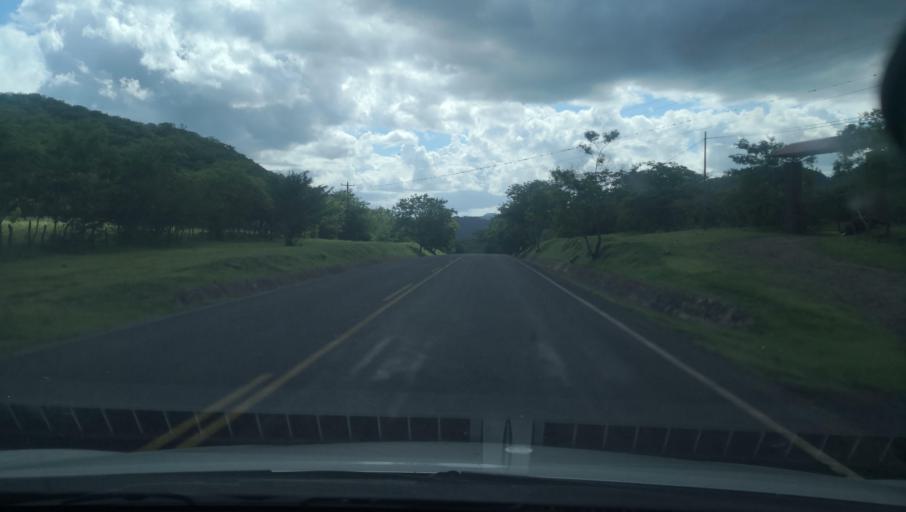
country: NI
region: Madriz
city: Somoto
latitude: 13.4660
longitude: -86.6470
